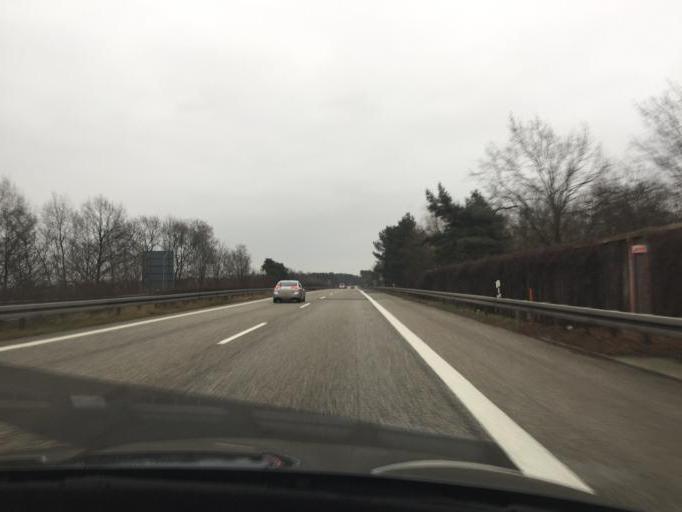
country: DE
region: Brandenburg
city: Lubbenau
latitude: 51.8300
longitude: 13.9884
